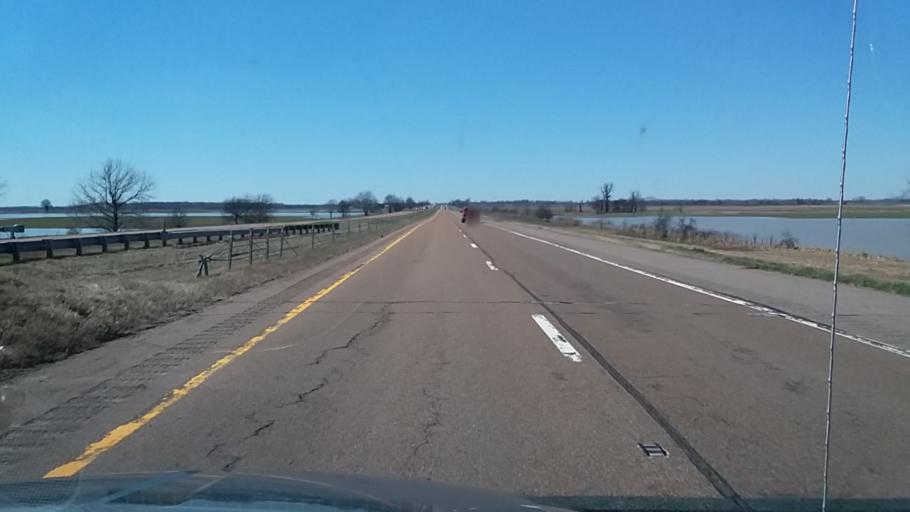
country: US
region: Missouri
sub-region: Pemiscot County
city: Caruthersville
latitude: 36.0855
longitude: -89.5507
